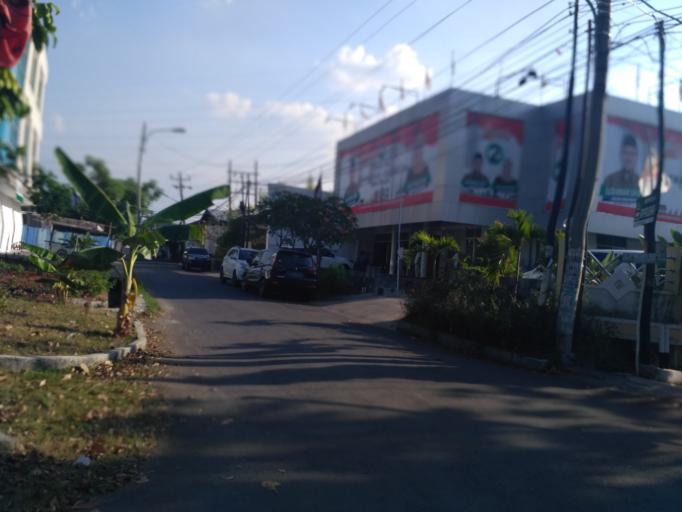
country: ID
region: Central Java
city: Semarang
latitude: -7.0009
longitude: 110.4490
